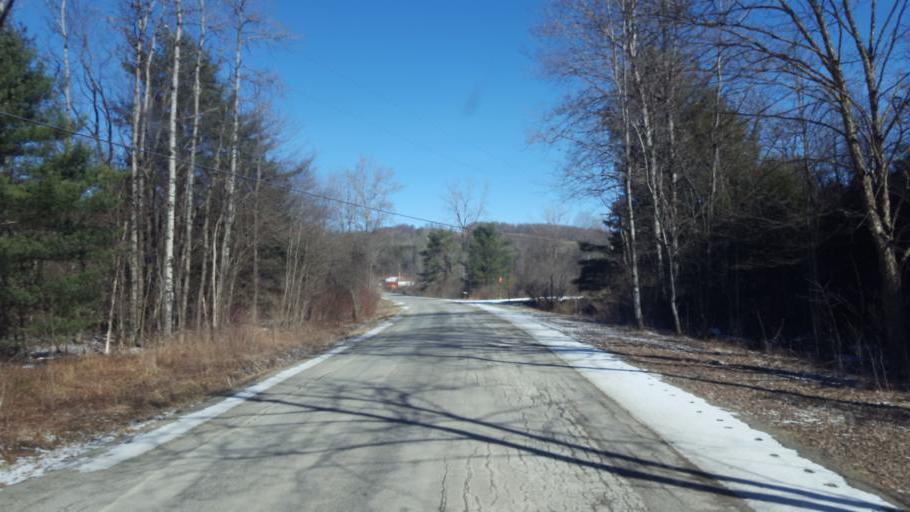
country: US
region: New York
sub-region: Allegany County
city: Wellsville
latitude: 42.0681
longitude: -77.9468
